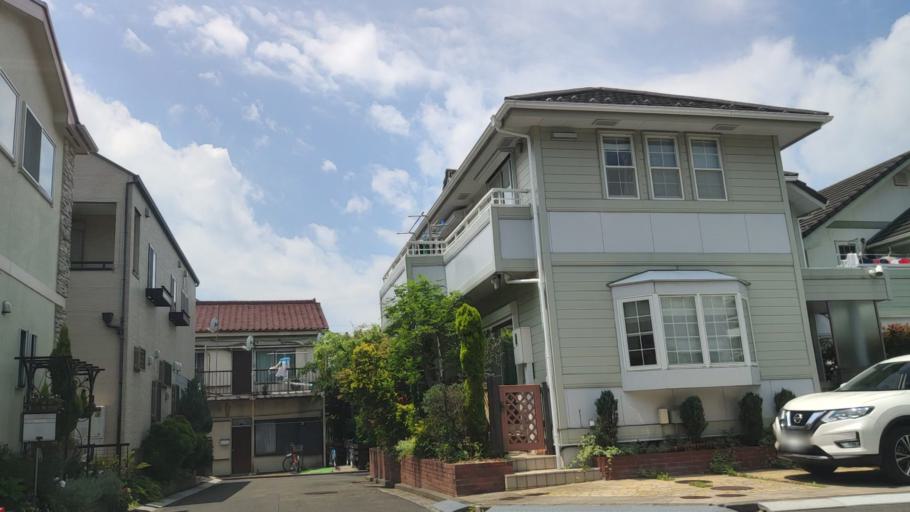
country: JP
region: Kanagawa
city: Yokohama
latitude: 35.4283
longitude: 139.6627
